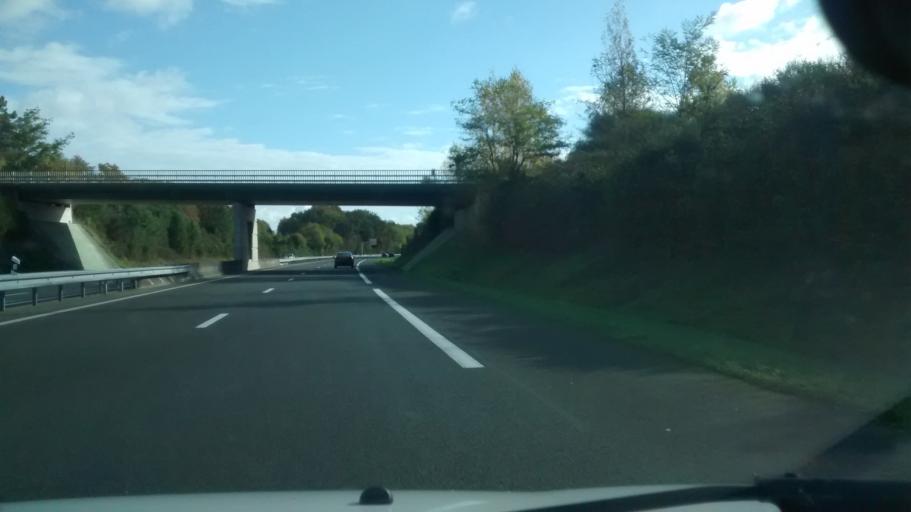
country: FR
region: Pays de la Loire
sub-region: Departement de Maine-et-Loire
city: Combree
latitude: 47.7154
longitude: -1.0127
